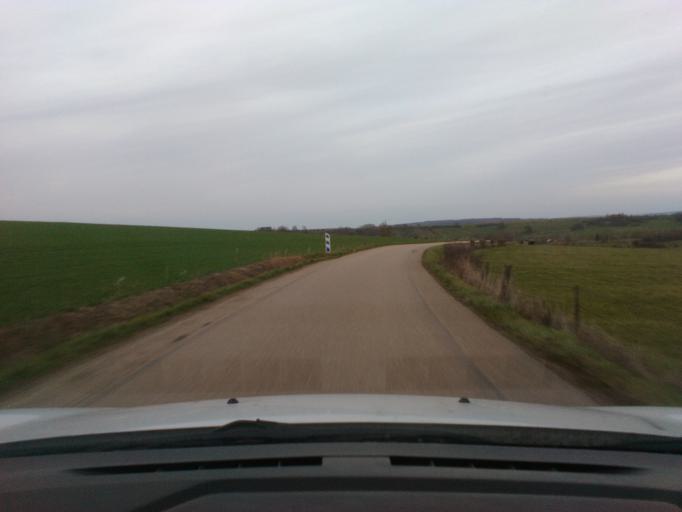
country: FR
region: Lorraine
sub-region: Departement des Vosges
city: Mirecourt
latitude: 48.3016
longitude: 6.0956
